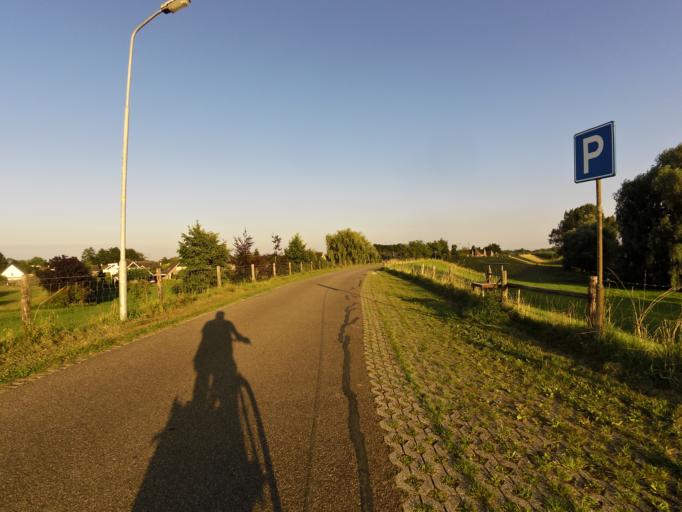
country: NL
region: Gelderland
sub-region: Gemeente Westervoort
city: Westervoort
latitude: 51.9287
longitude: 5.9851
